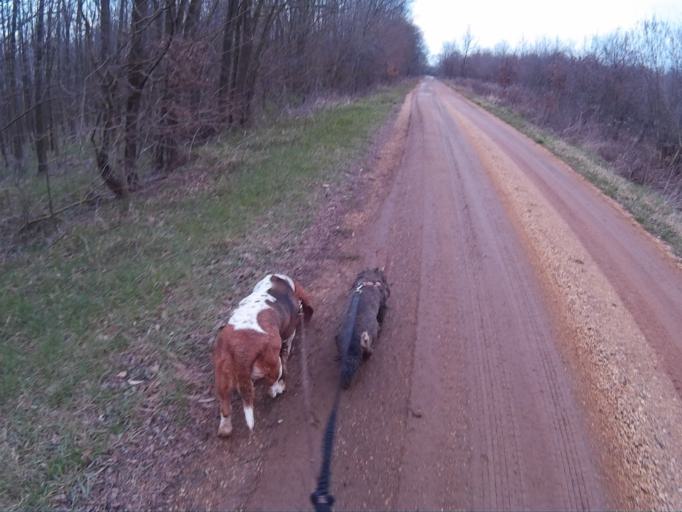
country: HU
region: Vas
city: Janoshaza
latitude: 47.1232
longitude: 17.0543
